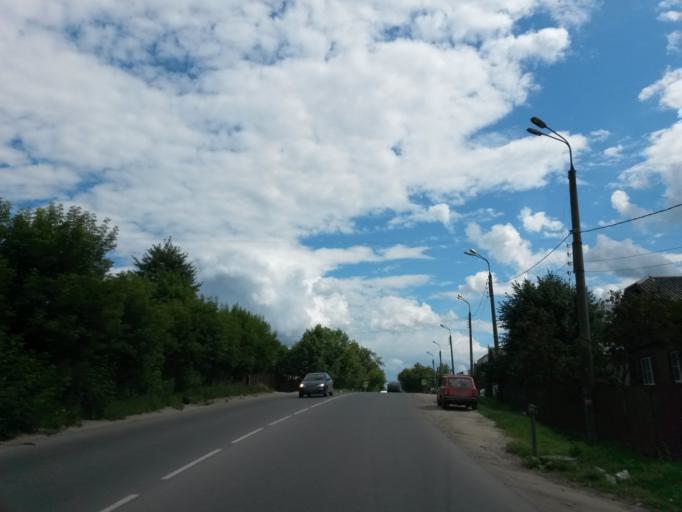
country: RU
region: Ivanovo
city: Novo-Talitsy
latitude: 57.0031
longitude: 40.8902
